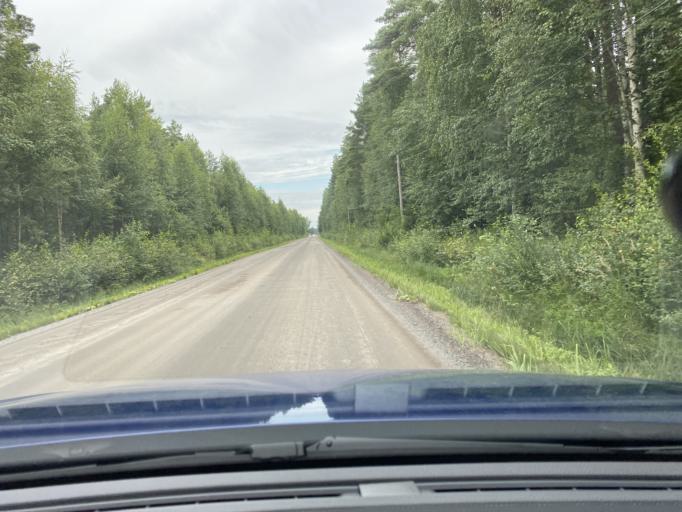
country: FI
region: Satakunta
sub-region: Rauma
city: Kiukainen
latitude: 61.1403
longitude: 21.9943
